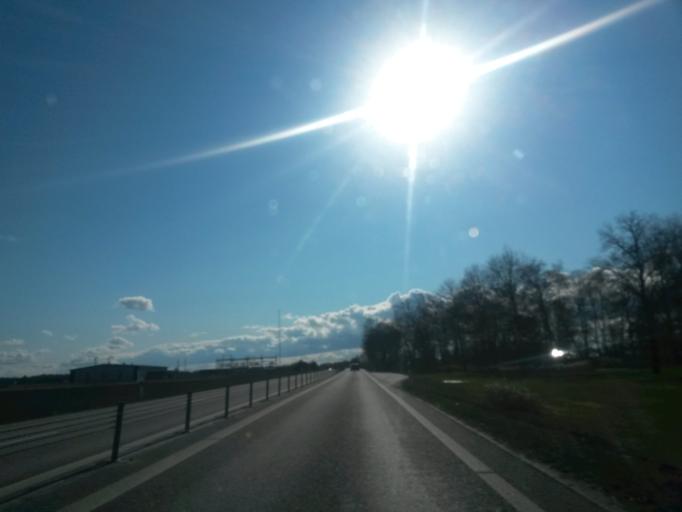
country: SE
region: Vaestra Goetaland
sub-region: Vara Kommun
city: Vara
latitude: 58.2608
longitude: 12.9813
